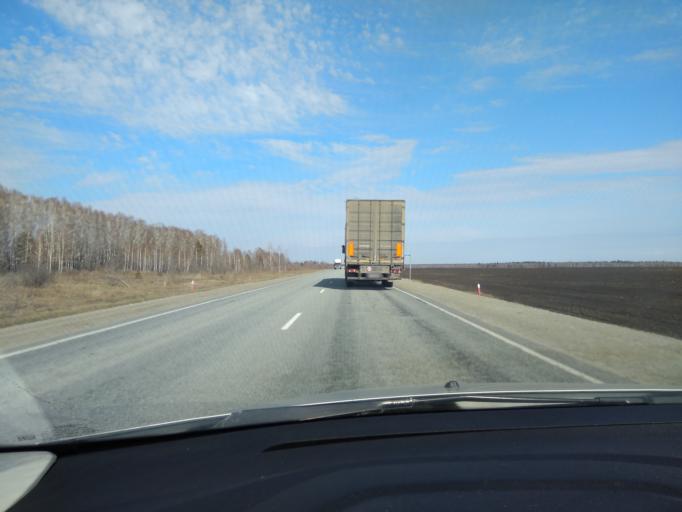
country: RU
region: Sverdlovsk
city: Tugulym
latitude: 57.0718
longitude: 64.6932
